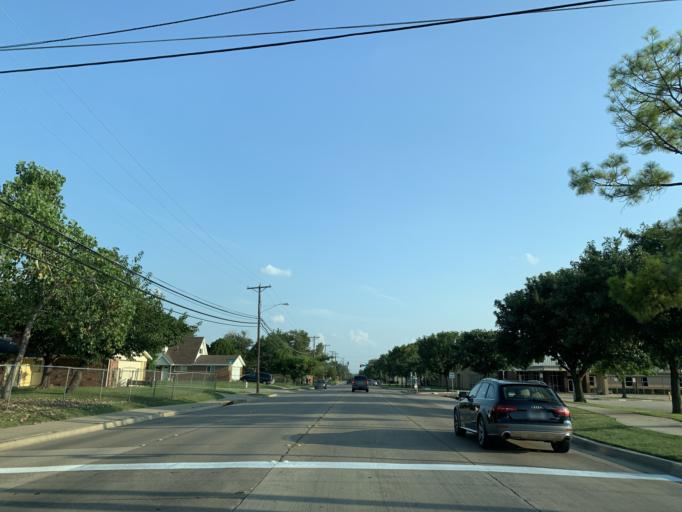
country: US
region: Texas
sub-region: Tarrant County
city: Hurst
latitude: 32.8192
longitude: -97.1865
